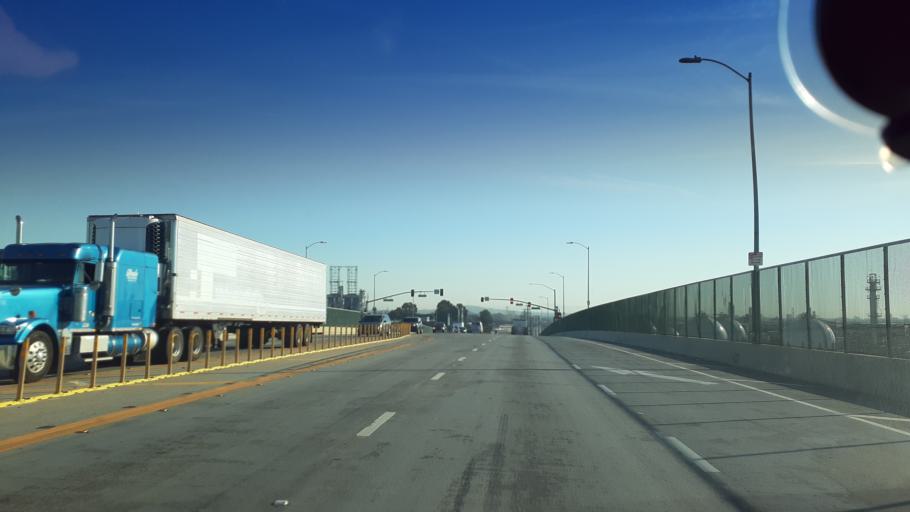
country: US
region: California
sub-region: Los Angeles County
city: Long Beach
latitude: 33.7912
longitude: -118.2396
